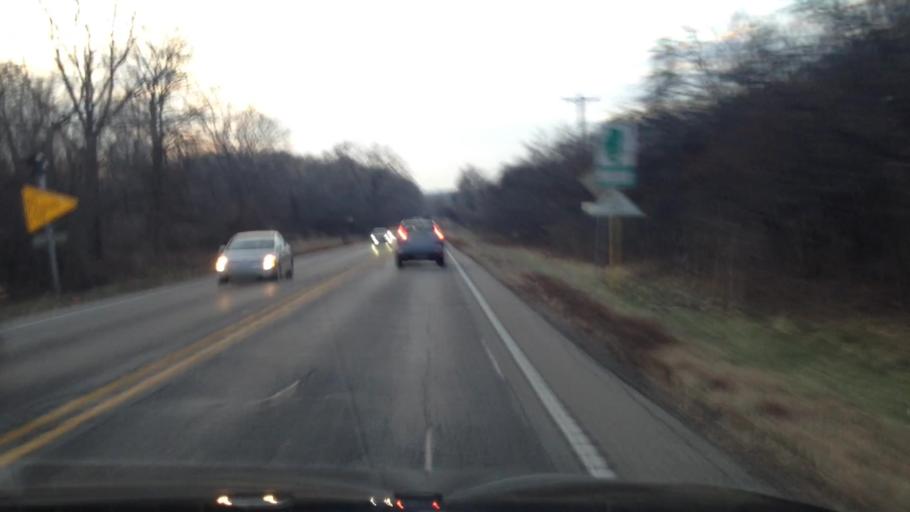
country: US
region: Illinois
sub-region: Cook County
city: Barrington Hills
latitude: 42.1188
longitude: -88.1972
